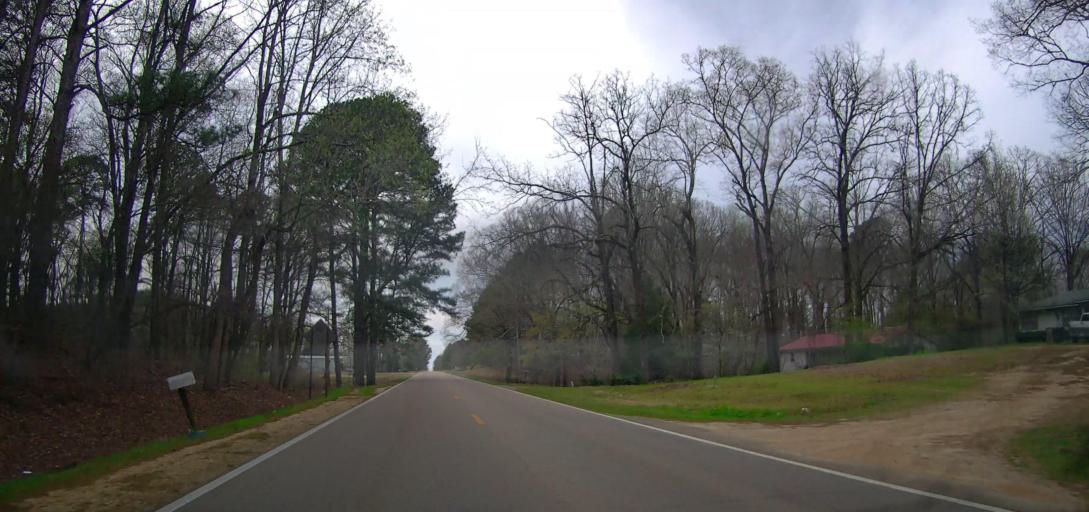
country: US
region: Mississippi
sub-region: Itawamba County
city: Mantachie
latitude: 34.2562
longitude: -88.4970
